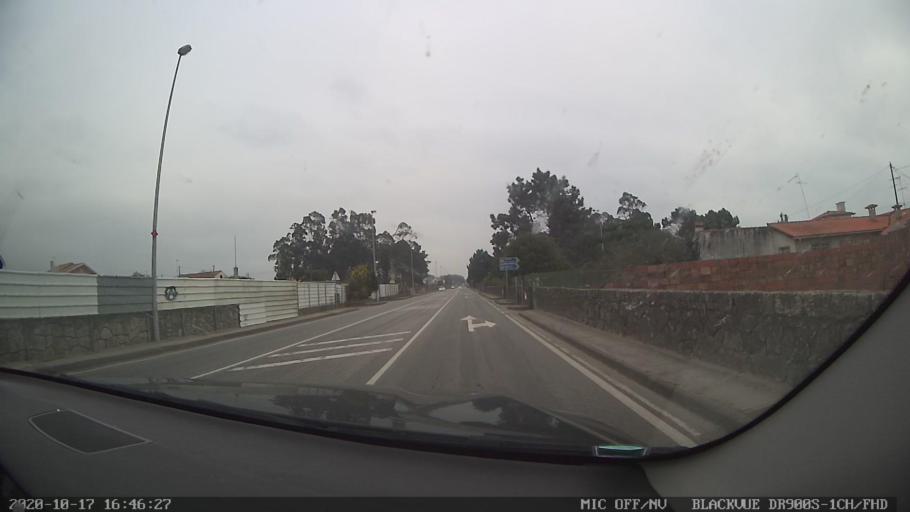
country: PT
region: Braga
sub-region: Esposende
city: Esposende
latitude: 41.5377
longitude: -8.7807
